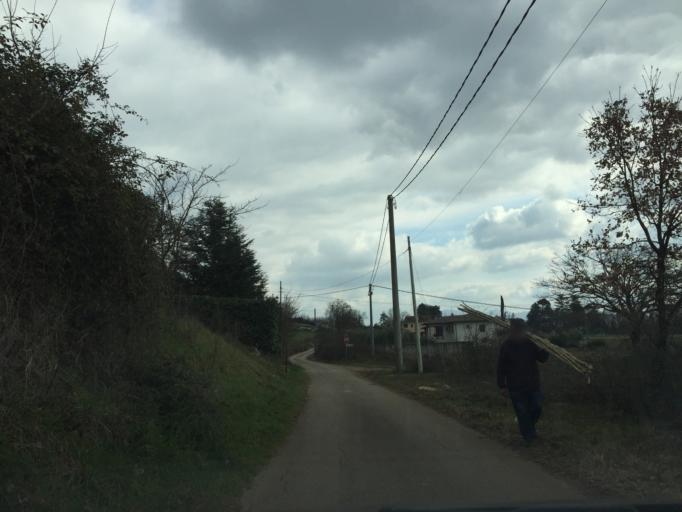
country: IT
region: Latium
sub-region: Provincia di Frosinone
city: Villa Santa Lucia
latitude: 41.4882
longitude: 13.7891
